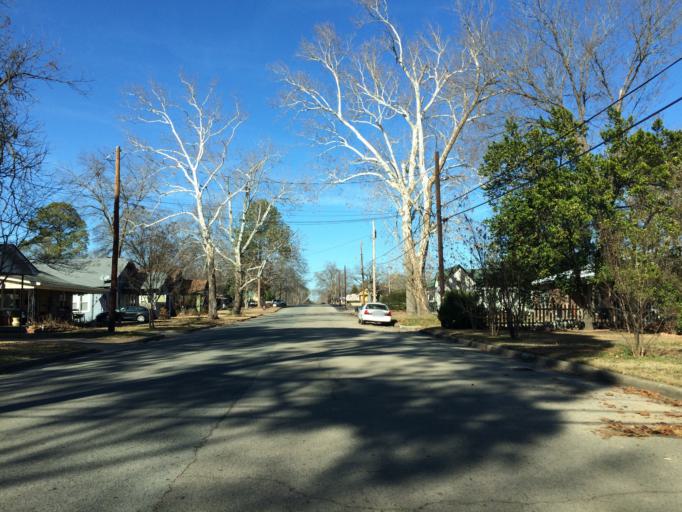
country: US
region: Texas
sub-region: Wood County
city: Mineola
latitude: 32.6666
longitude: -95.4858
